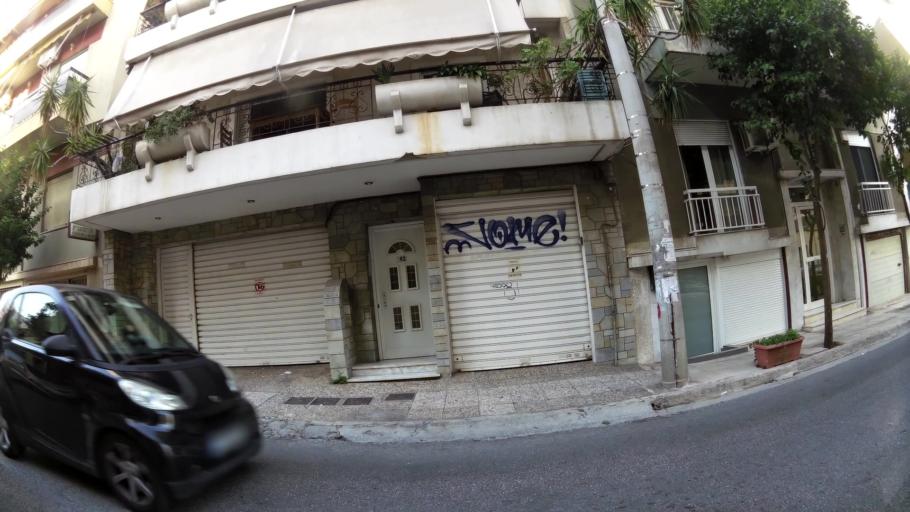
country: GR
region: Attica
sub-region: Nomos Piraios
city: Nikaia
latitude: 37.9743
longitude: 23.6459
